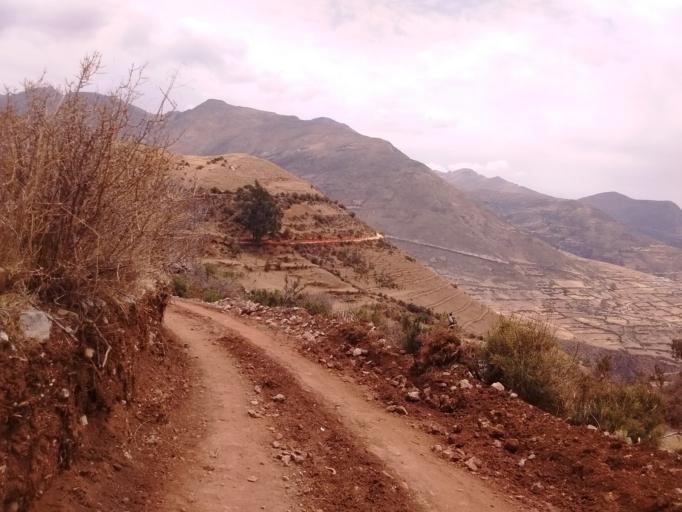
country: PE
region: Ayacucho
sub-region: Provincia de Victor Fajardo
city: Canaria
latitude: -13.8851
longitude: -73.9451
